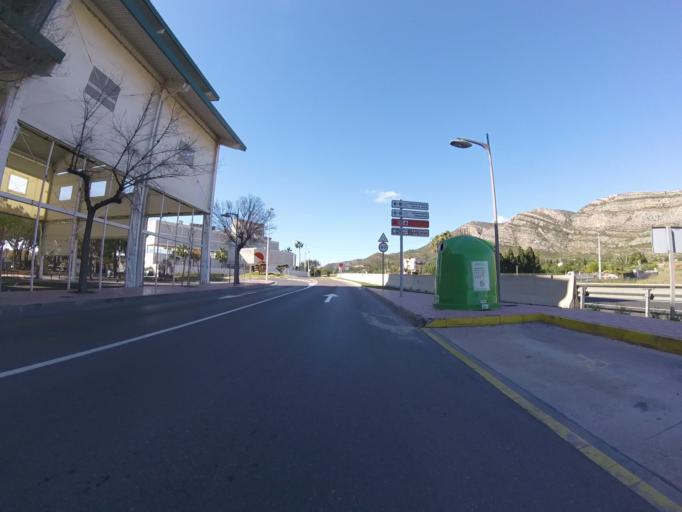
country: ES
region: Valencia
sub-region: Provincia de Castello
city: Orpesa/Oropesa del Mar
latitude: 40.0924
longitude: 0.1303
